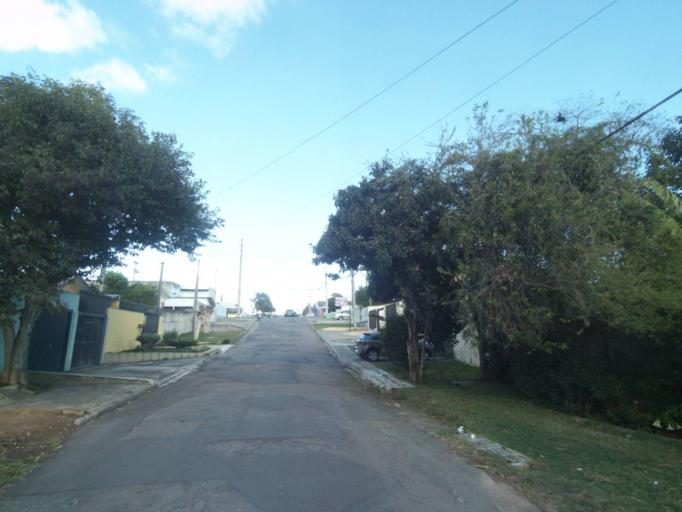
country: BR
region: Parana
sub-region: Sao Jose Dos Pinhais
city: Sao Jose dos Pinhais
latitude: -25.5246
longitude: -49.2880
